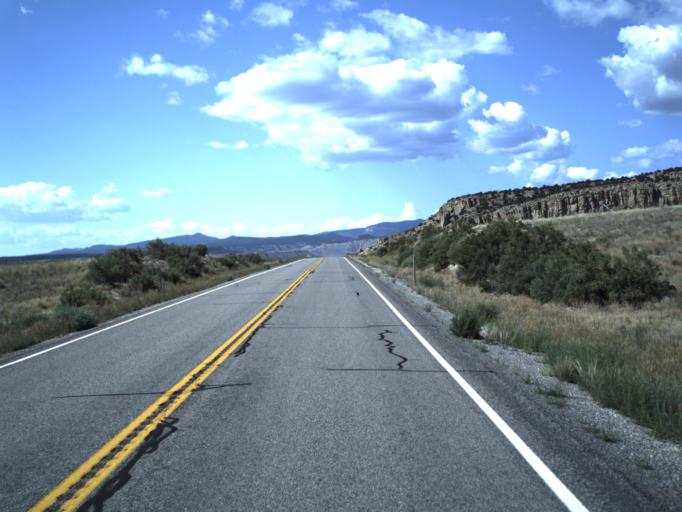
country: US
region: Utah
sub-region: Emery County
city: Ferron
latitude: 38.8382
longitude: -111.3165
